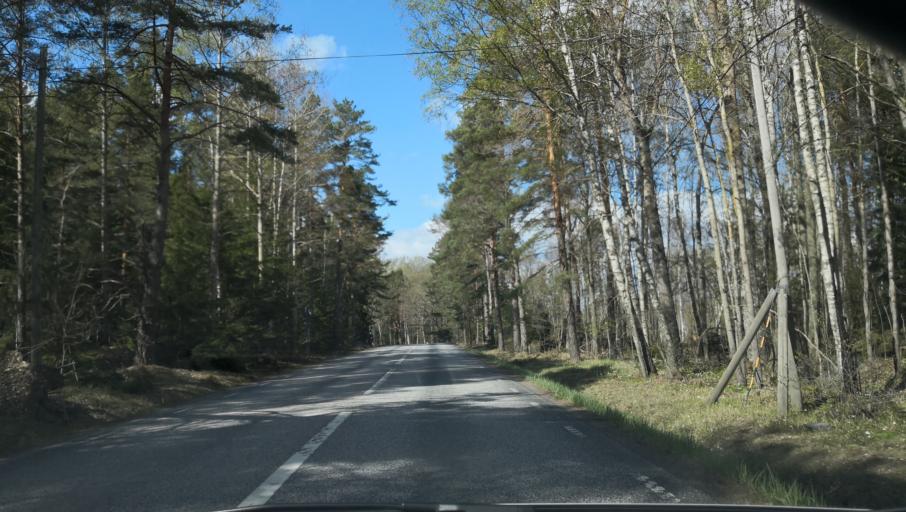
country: SE
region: Stockholm
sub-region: Varmdo Kommun
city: Hemmesta
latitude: 59.3803
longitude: 18.5232
